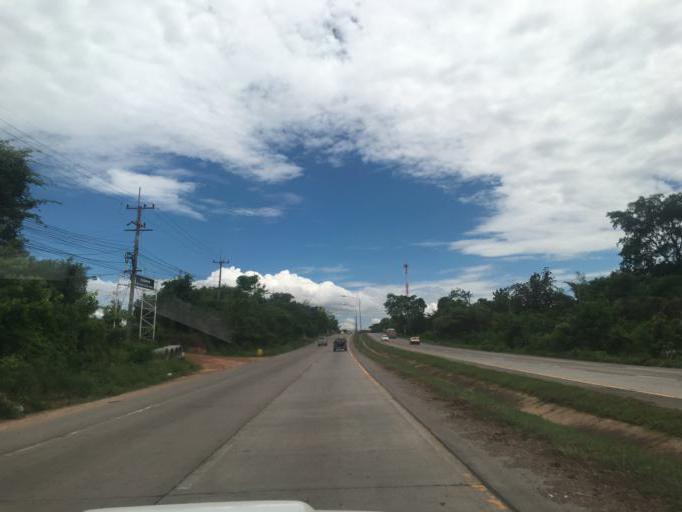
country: TH
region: Khon Kaen
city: Nam Phong
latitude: 16.6637
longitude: 102.8027
